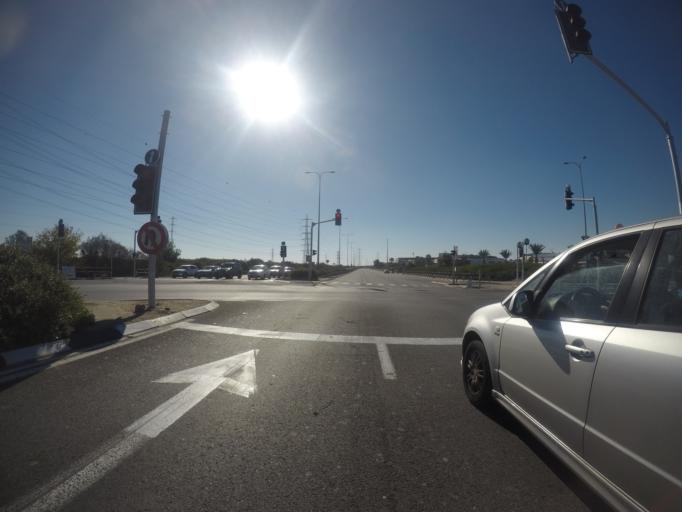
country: IL
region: Southern District
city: Ashdod
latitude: 31.7669
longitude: 34.6674
